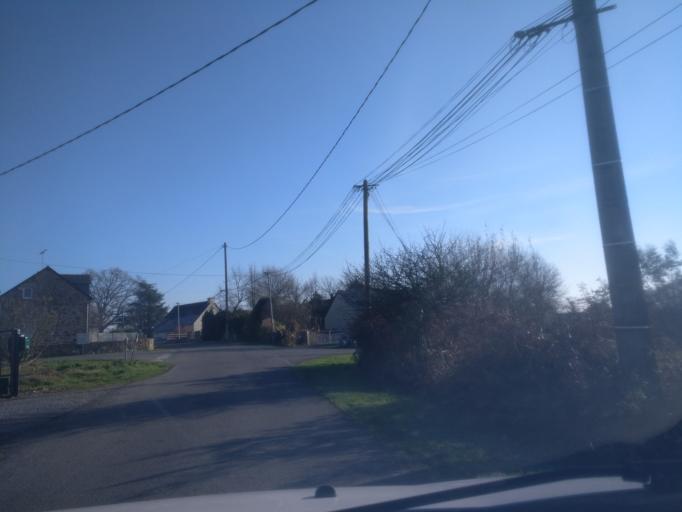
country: FR
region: Brittany
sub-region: Departement d'Ille-et-Vilaine
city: Livre-sur-Changeon
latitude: 48.2379
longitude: -1.3393
